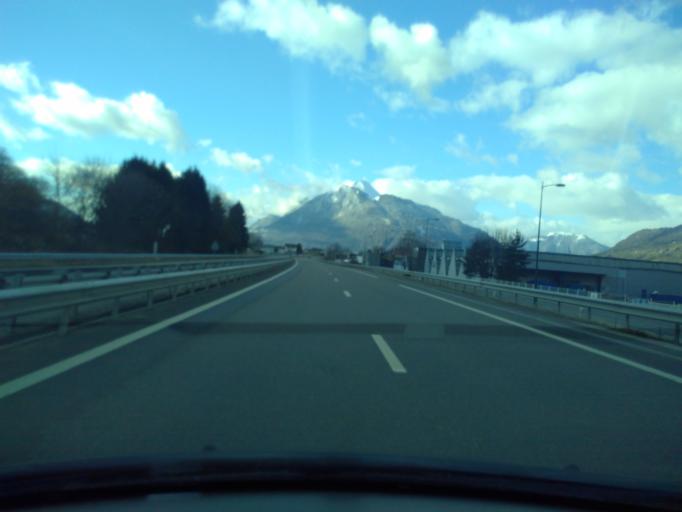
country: FR
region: Rhone-Alpes
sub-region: Departement de la Haute-Savoie
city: Cluses
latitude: 46.0596
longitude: 6.5669
